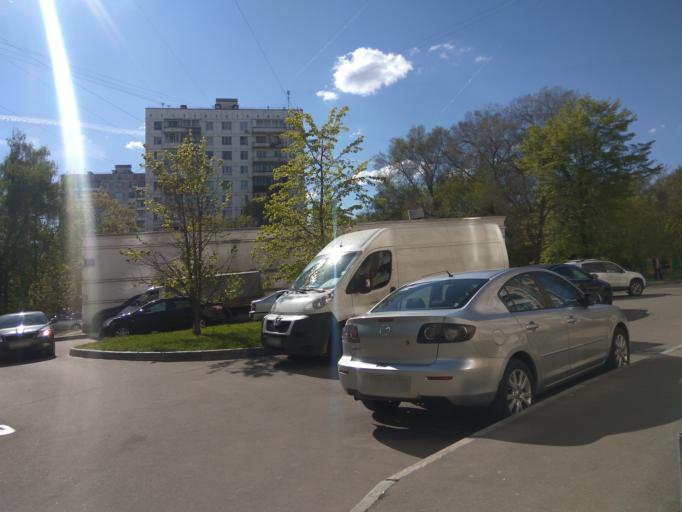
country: RU
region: Moscow
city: Kolomenskoye
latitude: 55.6771
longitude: 37.6755
